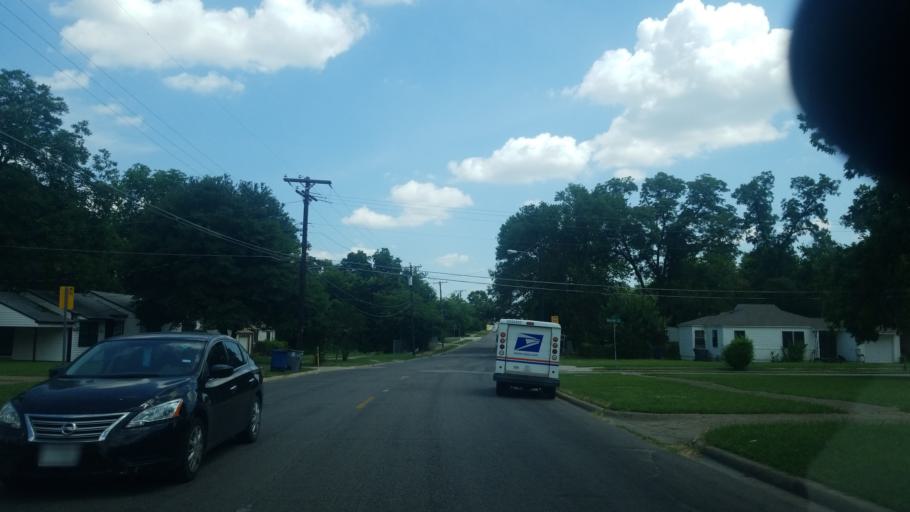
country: US
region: Texas
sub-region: Dallas County
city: Dallas
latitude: 32.7145
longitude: -96.7862
